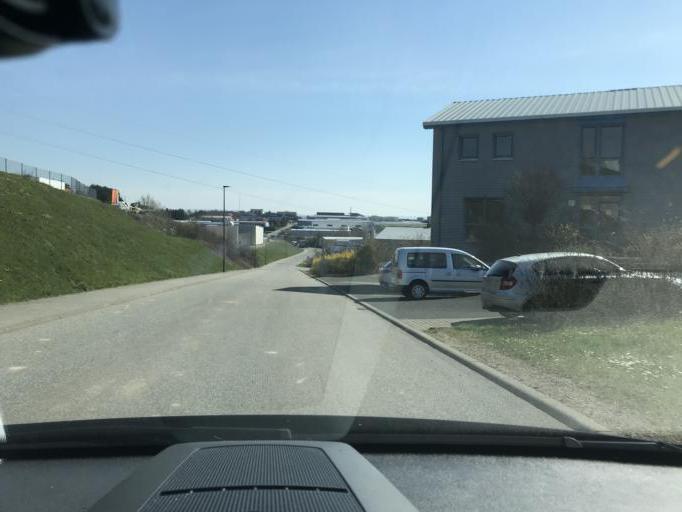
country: DE
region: Rheinland-Pfalz
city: Aach
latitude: 49.7739
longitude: 6.5805
